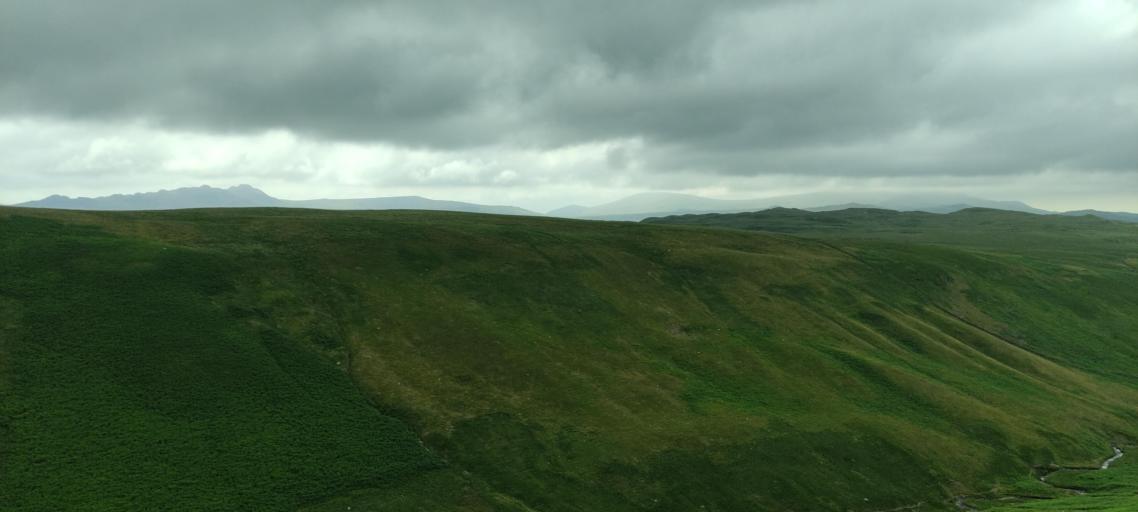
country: GB
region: England
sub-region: Cumbria
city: Seascale
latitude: 54.4191
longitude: -3.2803
